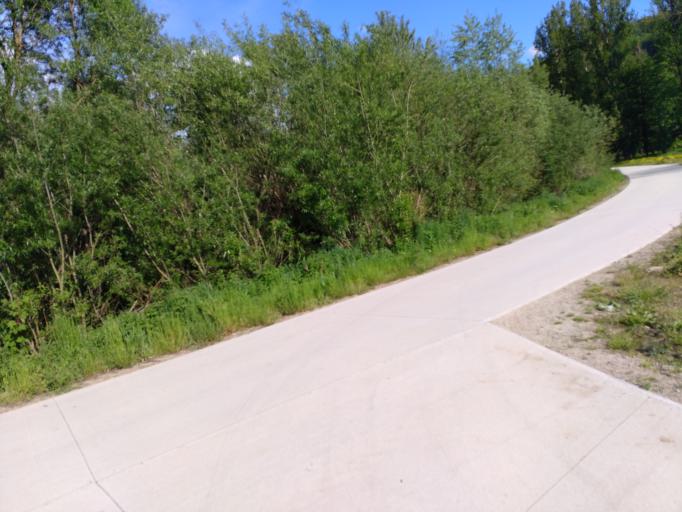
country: PL
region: Lesser Poland Voivodeship
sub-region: Powiat nowosadecki
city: Lacko
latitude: 49.5508
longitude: 20.4428
